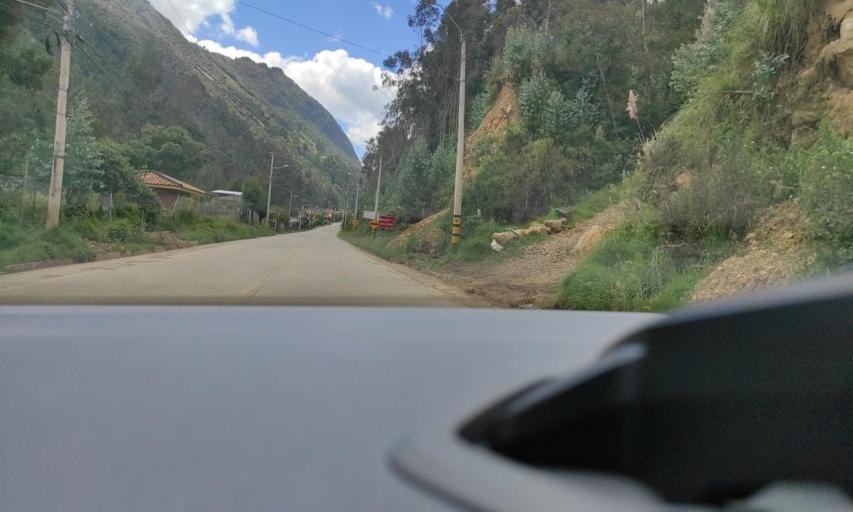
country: EC
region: Azuay
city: Cuenca
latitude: -2.8577
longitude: -79.0936
